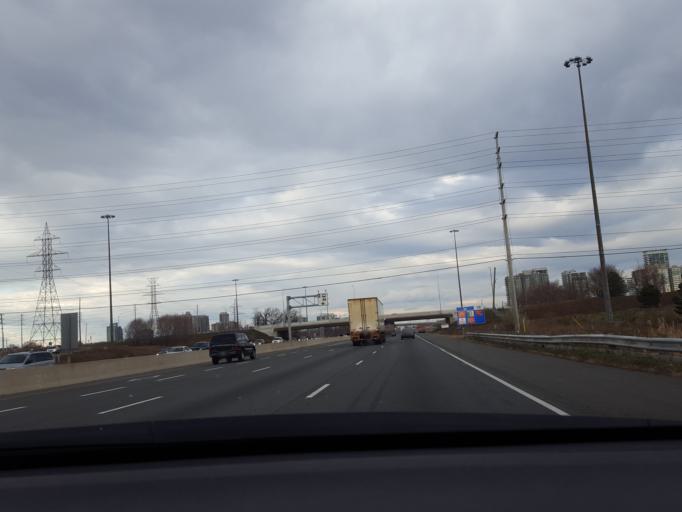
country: CA
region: Ontario
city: Mississauga
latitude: 43.5838
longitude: -79.6622
